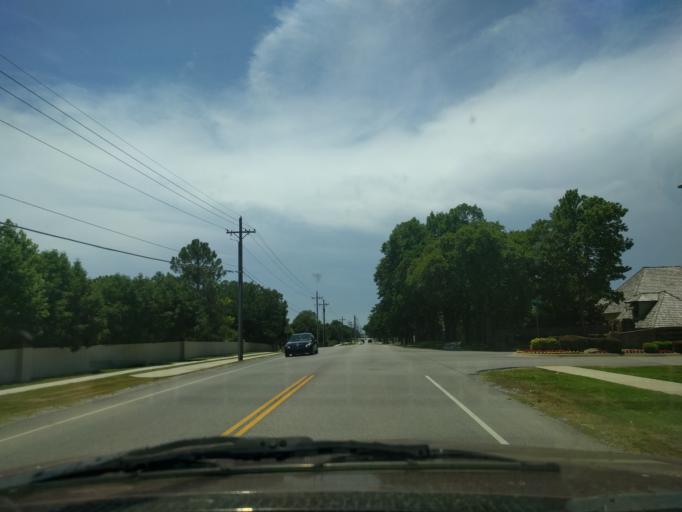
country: US
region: Oklahoma
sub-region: Tulsa County
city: Jenks
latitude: 36.0074
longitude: -95.9222
